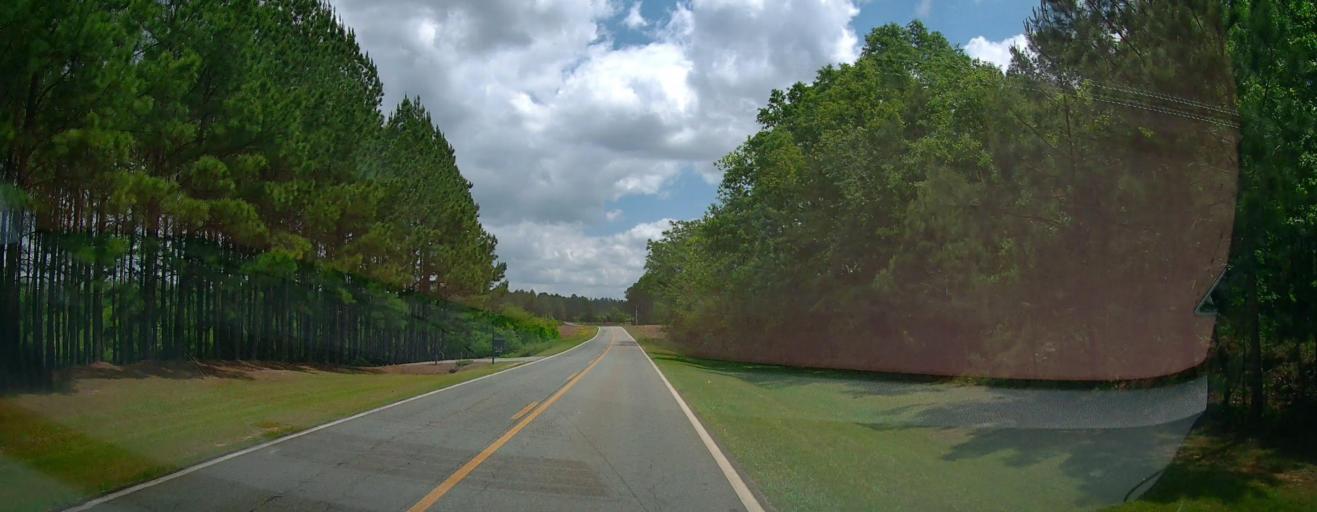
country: US
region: Georgia
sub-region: Laurens County
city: Dublin
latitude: 32.5994
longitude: -83.0049
